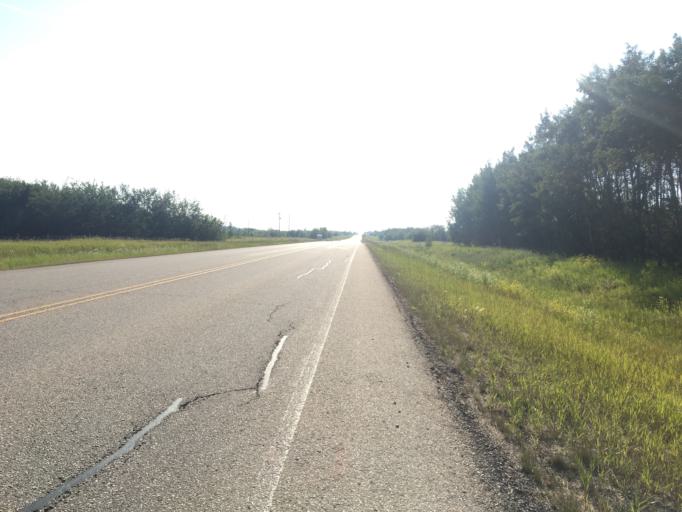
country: CA
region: Alberta
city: Sexsmith
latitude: 55.3742
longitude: -118.7933
